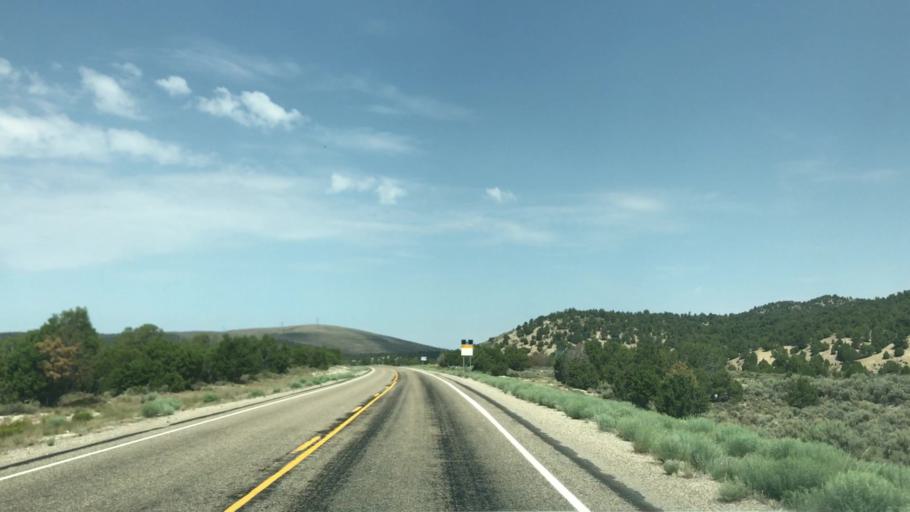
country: US
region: Nevada
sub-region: White Pine County
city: Ely
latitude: 39.3799
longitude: -115.0655
